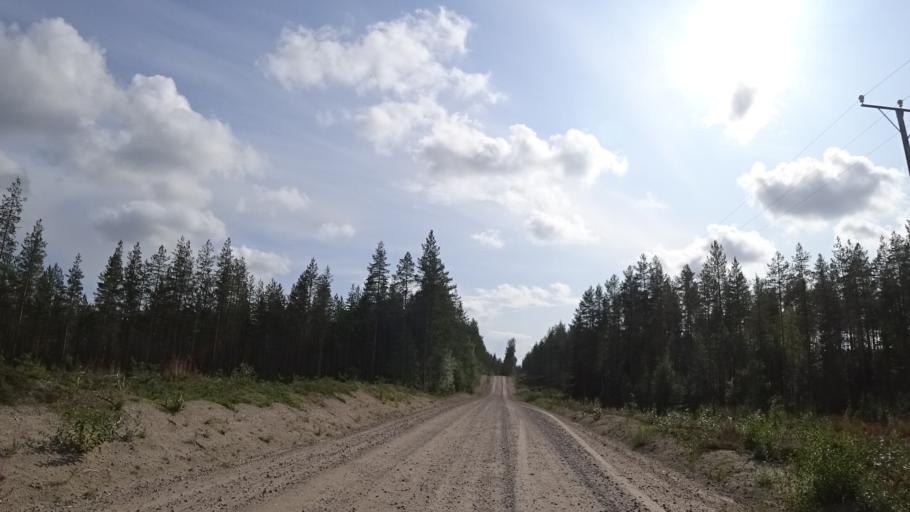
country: FI
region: North Karelia
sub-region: Pielisen Karjala
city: Lieksa
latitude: 63.5592
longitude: 30.0664
